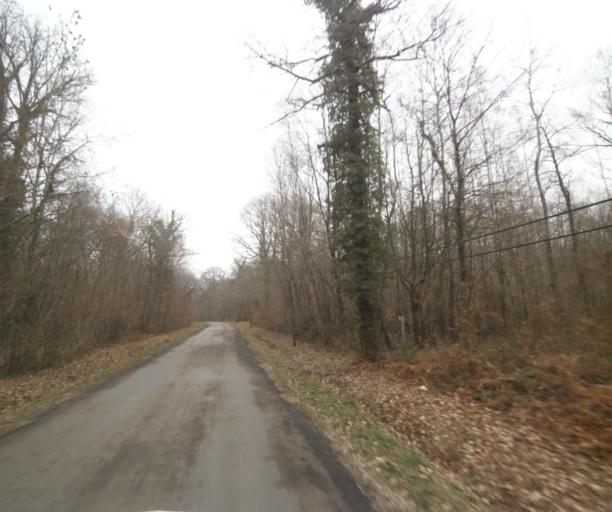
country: FR
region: Champagne-Ardenne
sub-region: Departement de la Haute-Marne
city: Wassy
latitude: 48.5226
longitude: 4.9751
